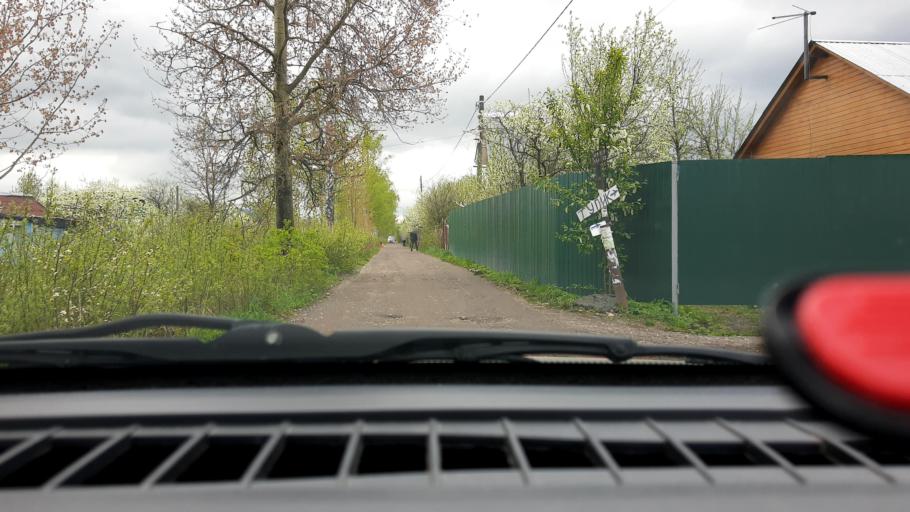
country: RU
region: Nizjnij Novgorod
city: Gorbatovka
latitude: 56.2432
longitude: 43.8125
